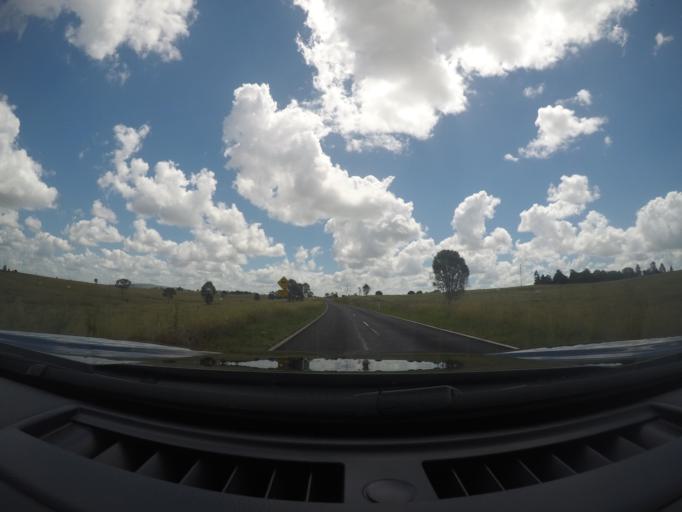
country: AU
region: Queensland
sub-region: Moreton Bay
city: Woodford
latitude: -27.1392
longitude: 152.5045
